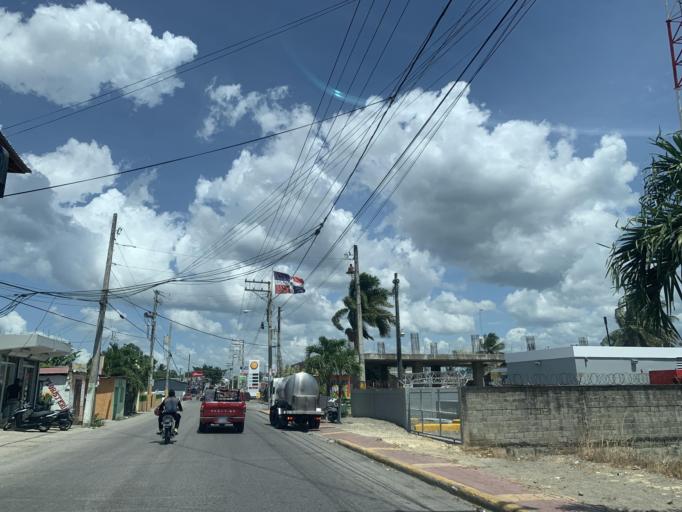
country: DO
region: Espaillat
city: Jamao al Norte
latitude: 19.6705
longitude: -70.3707
